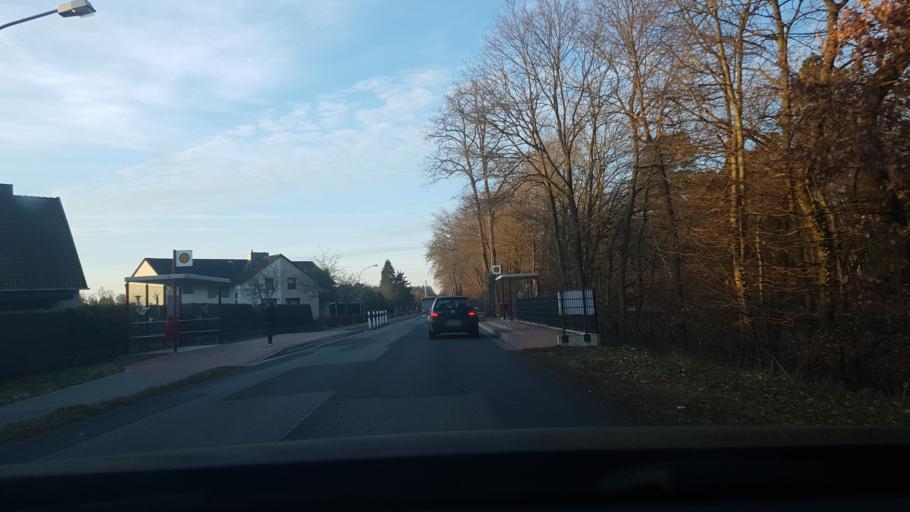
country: DE
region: Lower Saxony
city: Gifhorn
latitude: 52.5063
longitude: 10.5765
